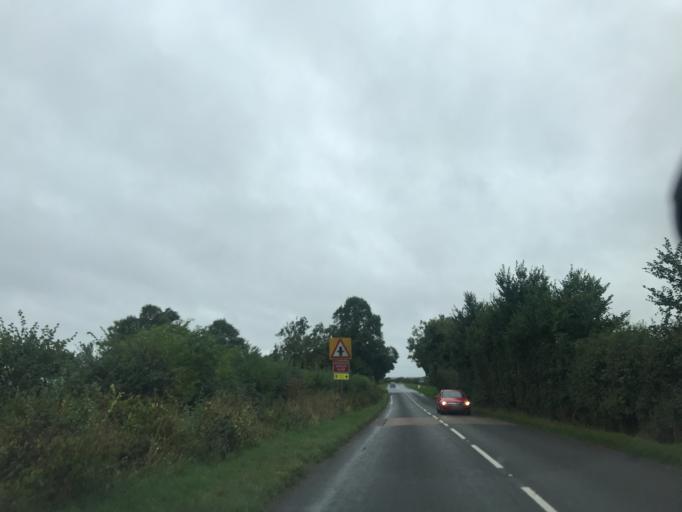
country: GB
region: England
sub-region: Buckinghamshire
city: Stone
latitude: 51.7992
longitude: -0.8531
